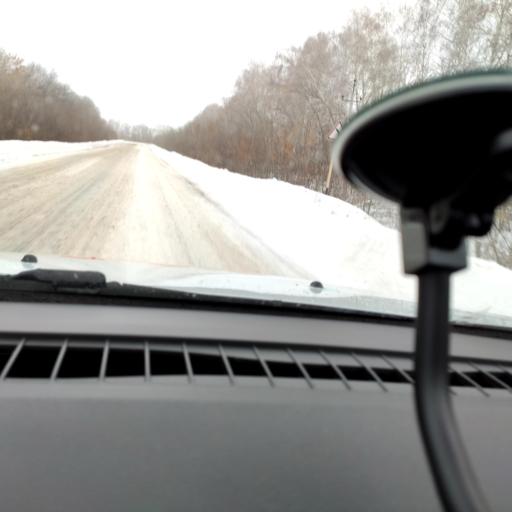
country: RU
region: Samara
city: Dubovyy Umet
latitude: 53.0316
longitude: 50.2286
